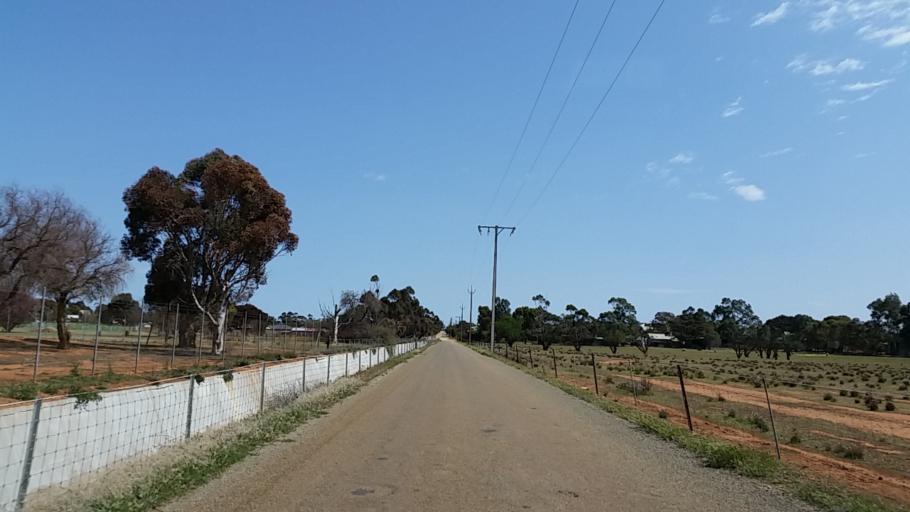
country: AU
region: South Australia
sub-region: Peterborough
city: Peterborough
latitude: -32.9693
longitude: 138.8451
